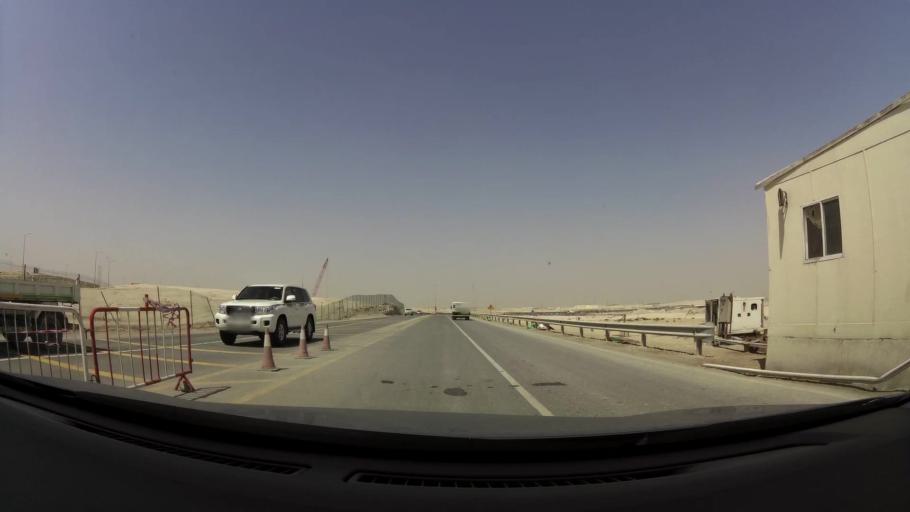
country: QA
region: Baladiyat Umm Salal
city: Umm Salal Muhammad
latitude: 25.3960
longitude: 51.4984
